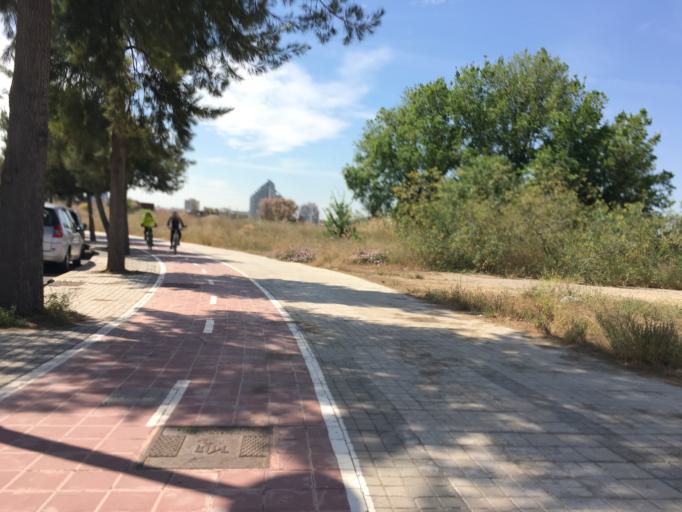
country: ES
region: Valencia
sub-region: Provincia de Valencia
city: Mislata
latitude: 39.4810
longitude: -0.4081
